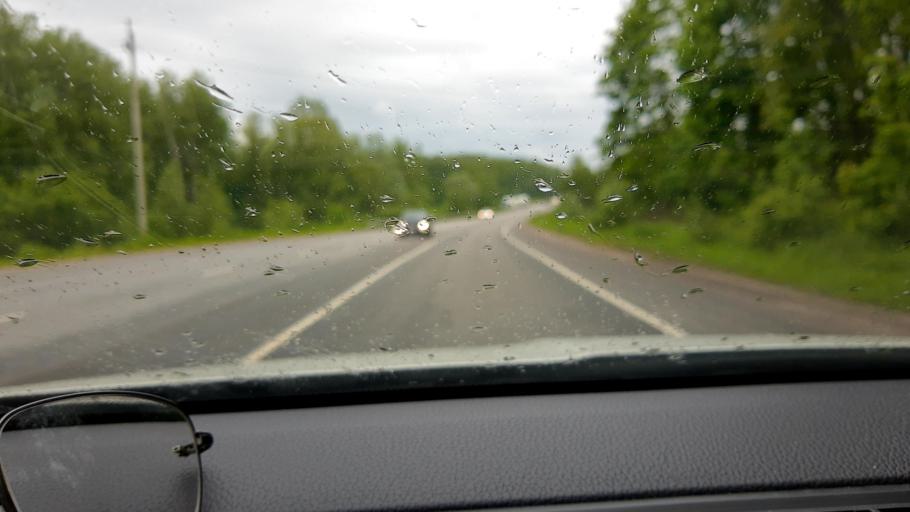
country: RU
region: Moskovskaya
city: Gorki-Leninskiye
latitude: 55.5231
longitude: 37.7904
